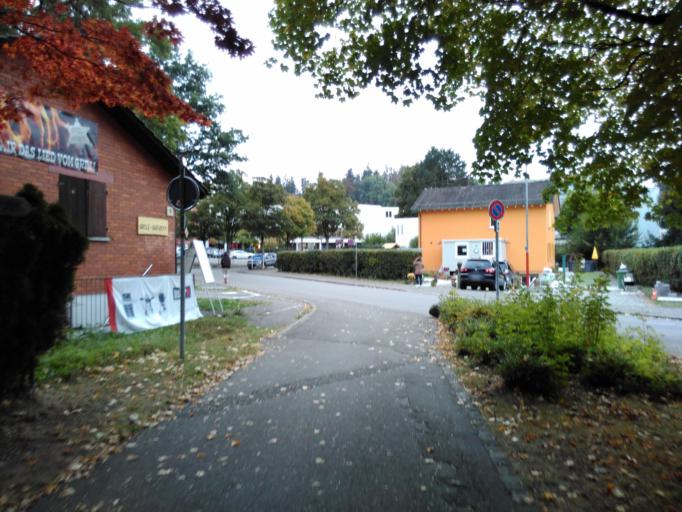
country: CH
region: Zurich
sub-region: Bezirk Buelach
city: Kloten / Holberg
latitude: 47.4455
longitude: 8.5818
